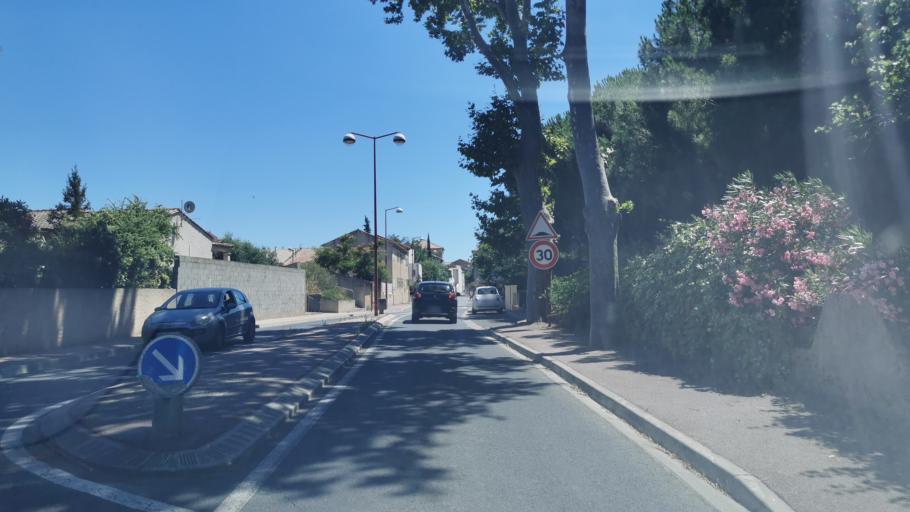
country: FR
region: Languedoc-Roussillon
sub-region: Departement de l'Aude
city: Vinassan
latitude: 43.2056
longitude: 3.0746
